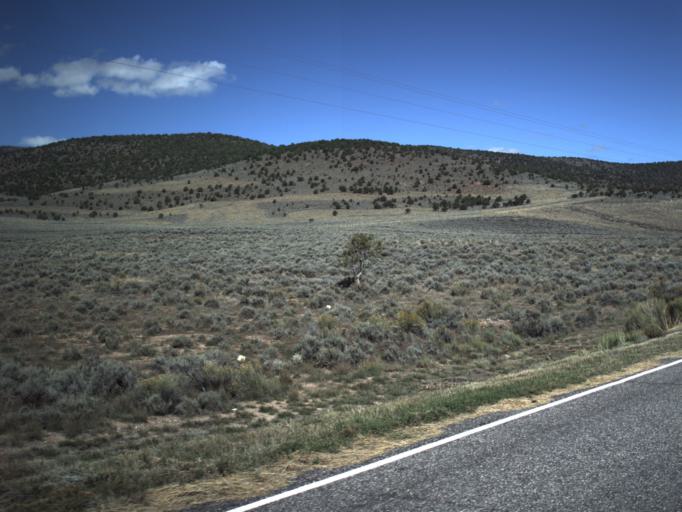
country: US
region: Utah
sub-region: Sevier County
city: Monroe
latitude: 38.5224
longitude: -111.8811
